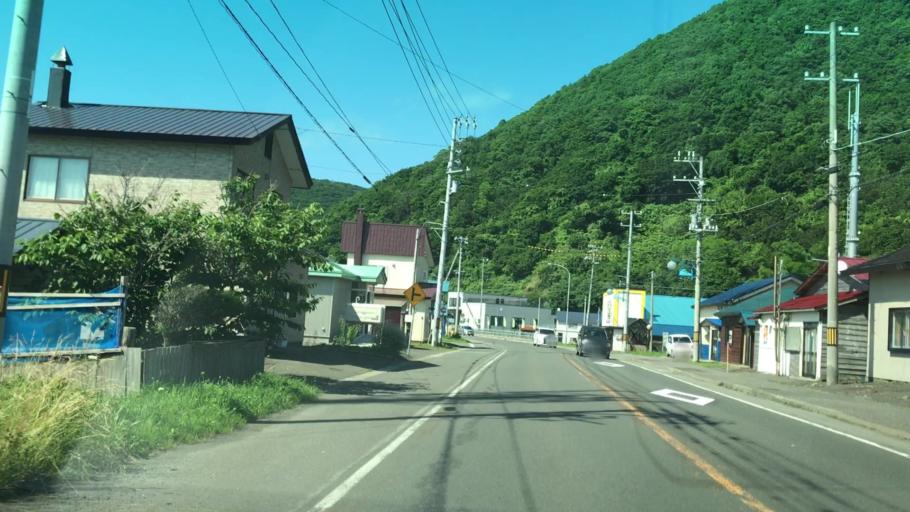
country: JP
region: Hokkaido
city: Iwanai
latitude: 43.0998
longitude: 140.4610
